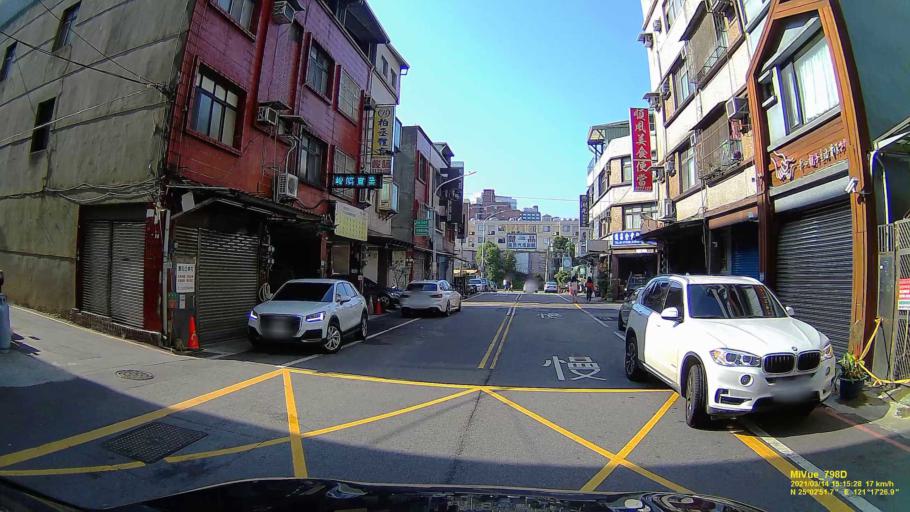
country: TW
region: Taiwan
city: Taoyuan City
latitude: 25.0478
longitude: 121.2908
